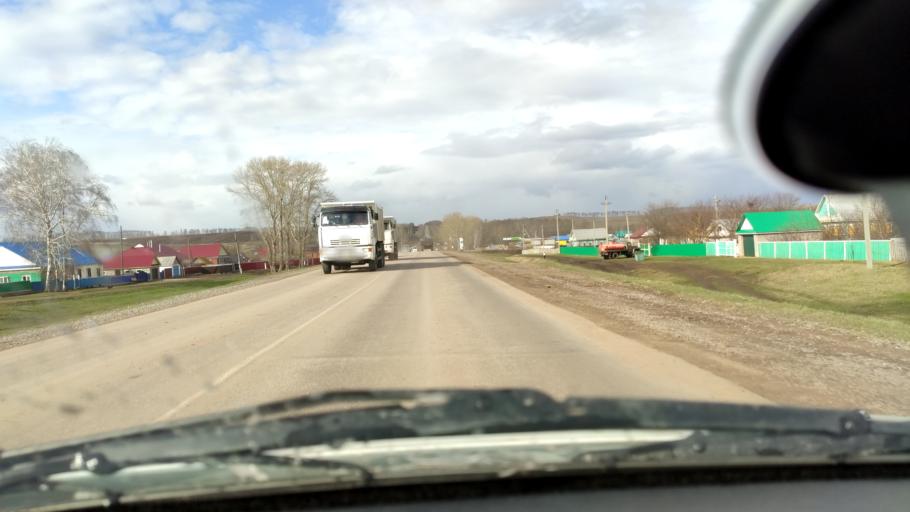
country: RU
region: Bashkortostan
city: Buzdyak
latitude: 54.6843
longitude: 54.5537
